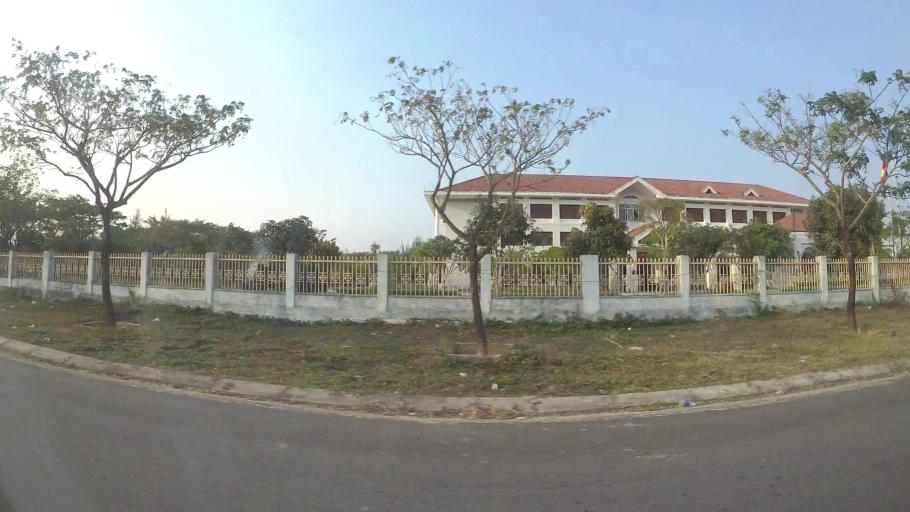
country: VN
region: Da Nang
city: Ngu Hanh Son
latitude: 15.9779
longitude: 108.2449
